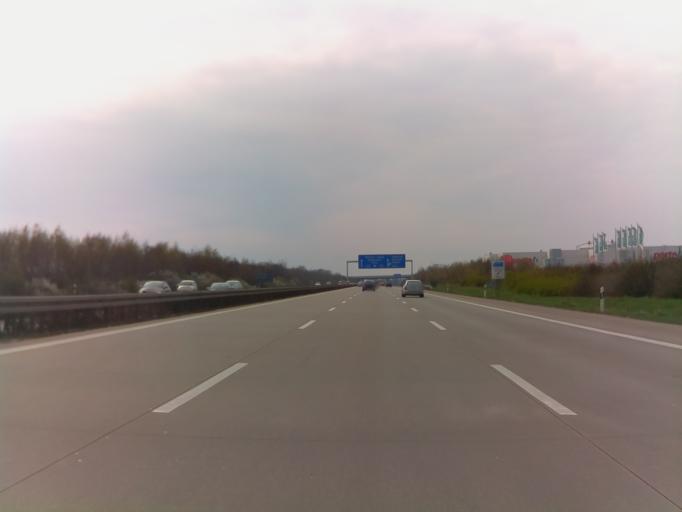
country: DE
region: Saxony
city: Wiedemar
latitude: 51.4737
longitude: 12.2150
